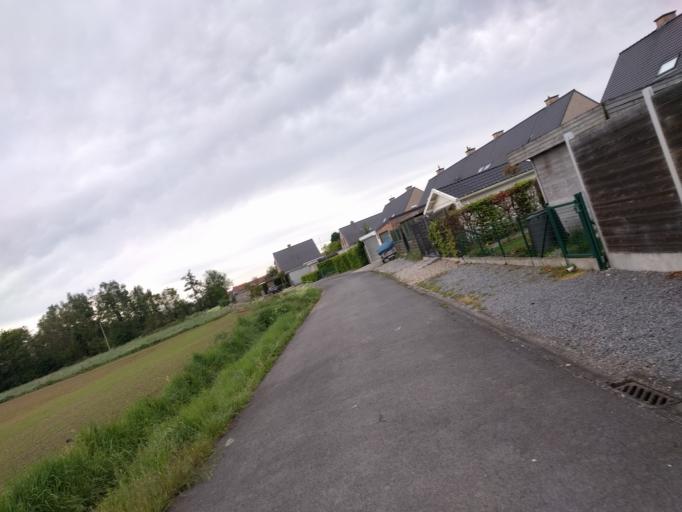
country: BE
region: Flanders
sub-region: Provincie West-Vlaanderen
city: Wevelgem
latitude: 50.8071
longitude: 3.1581
